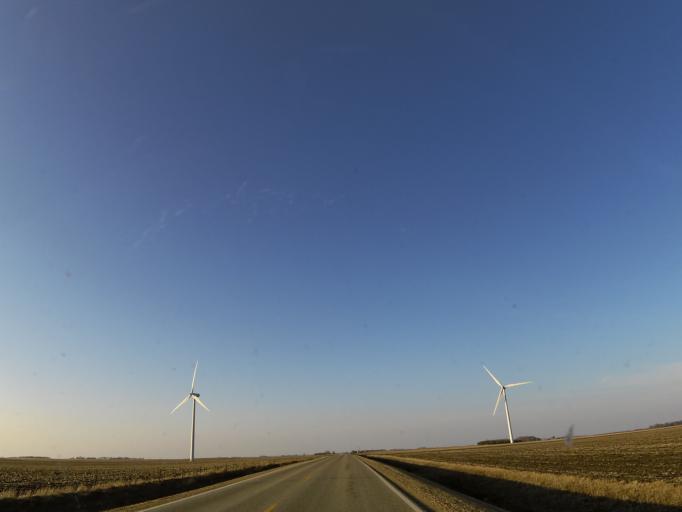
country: US
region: Iowa
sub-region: Worth County
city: Northwood
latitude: 43.4163
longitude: -93.1243
